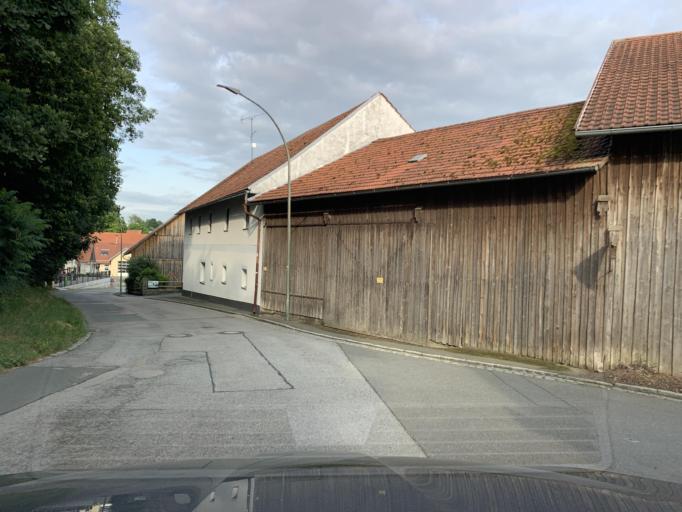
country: DE
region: Bavaria
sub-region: Upper Palatinate
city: Dieterskirchen
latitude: 49.3983
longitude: 12.4162
